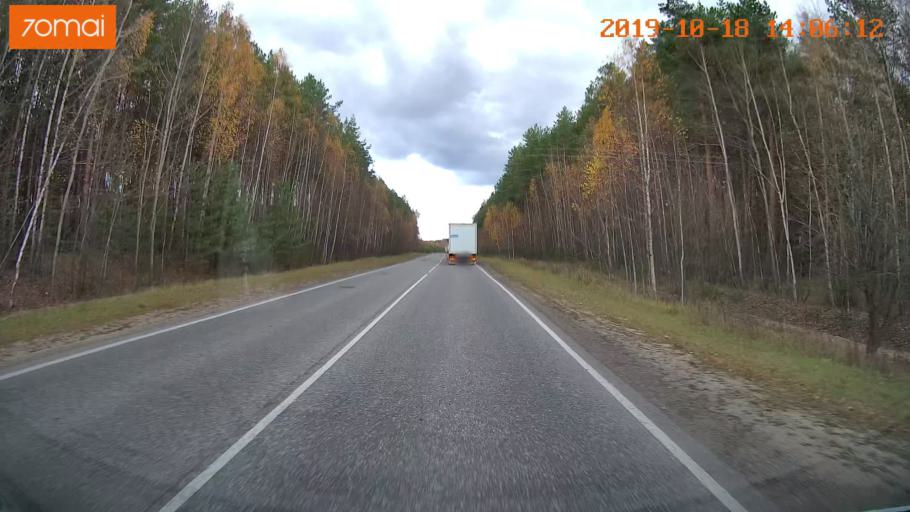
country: RU
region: Rjazan
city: Spas-Klepiki
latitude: 55.1423
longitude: 40.1492
